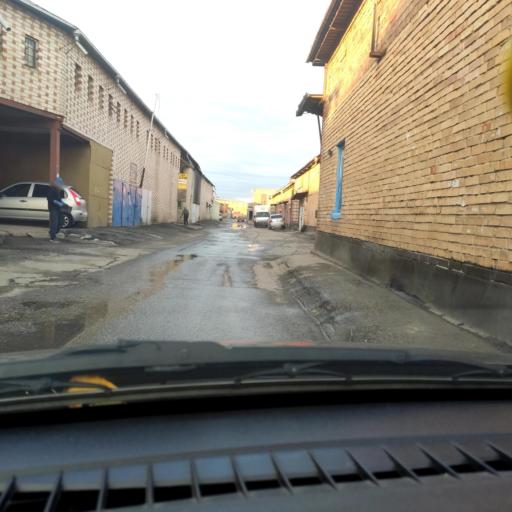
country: RU
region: Samara
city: Tol'yatti
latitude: 53.5389
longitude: 49.2952
